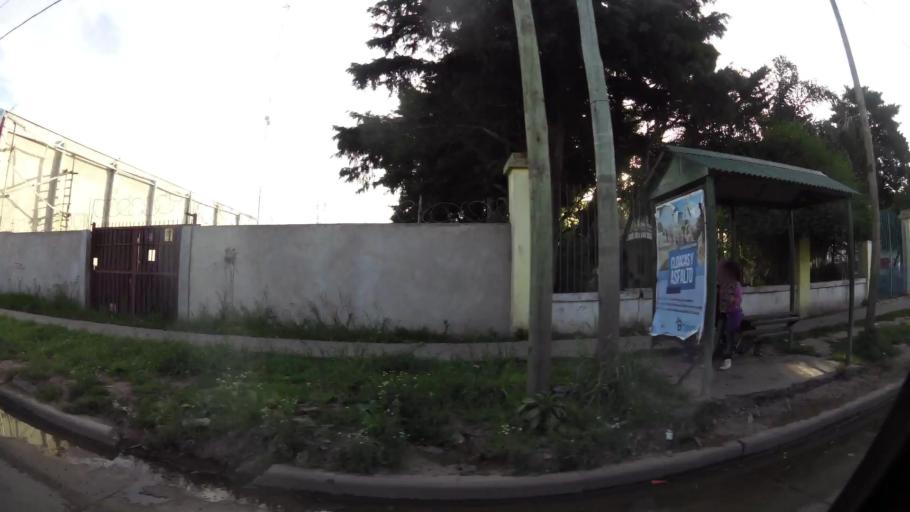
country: AR
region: Buenos Aires
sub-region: Partido de Almirante Brown
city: Adrogue
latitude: -34.7895
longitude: -58.3267
